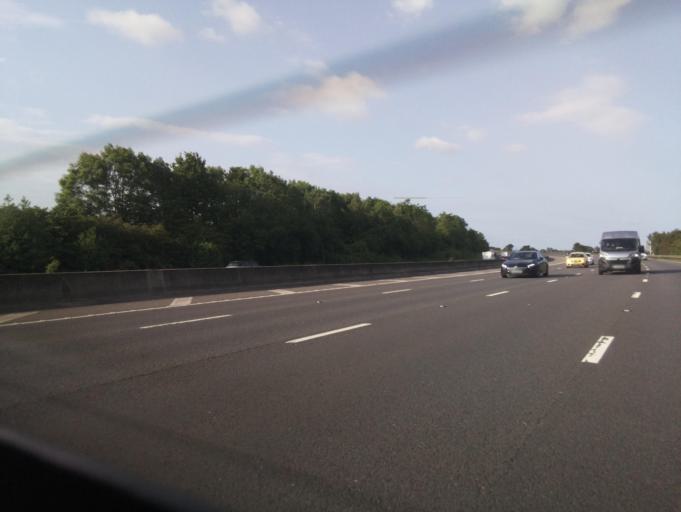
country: GB
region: England
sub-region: Worcestershire
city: Droitwich
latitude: 52.2697
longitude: -2.1255
